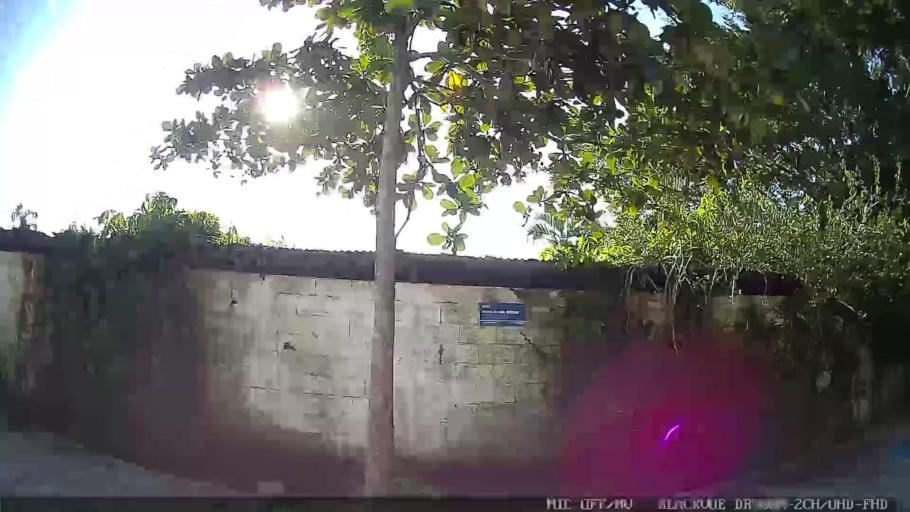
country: BR
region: Sao Paulo
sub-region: Itanhaem
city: Itanhaem
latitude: -24.1750
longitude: -46.8169
